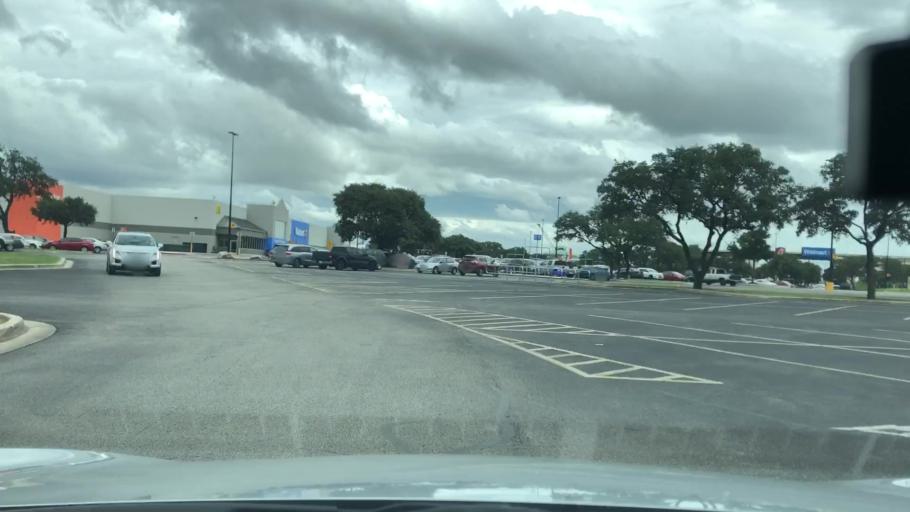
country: US
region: Texas
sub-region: Bexar County
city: Hollywood Park
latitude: 29.6119
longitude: -98.4729
